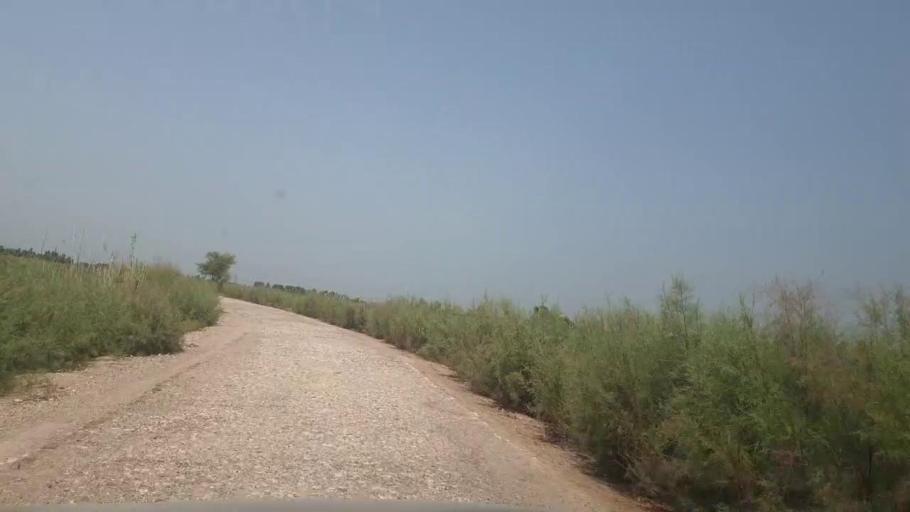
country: PK
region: Sindh
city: Lakhi
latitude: 27.8493
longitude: 68.6247
